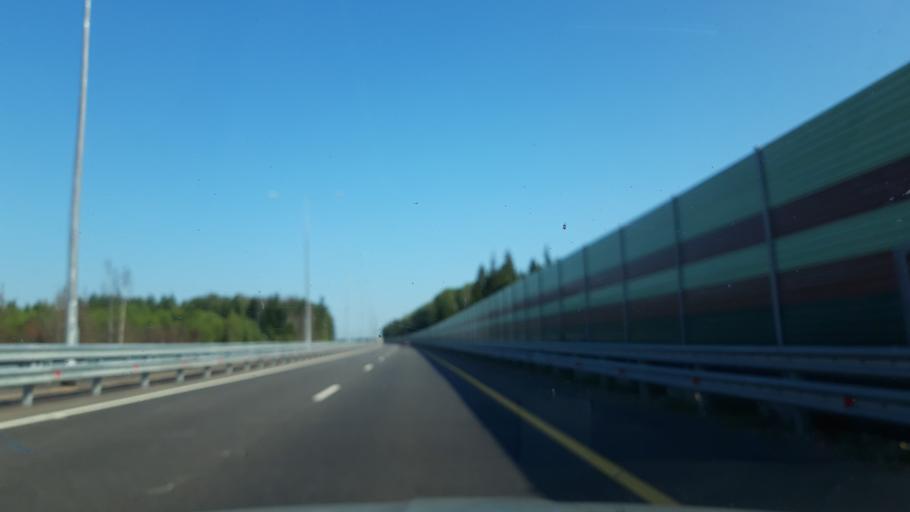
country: RU
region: Moskovskaya
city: Spas-Zaulok
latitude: 56.4825
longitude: 36.5373
